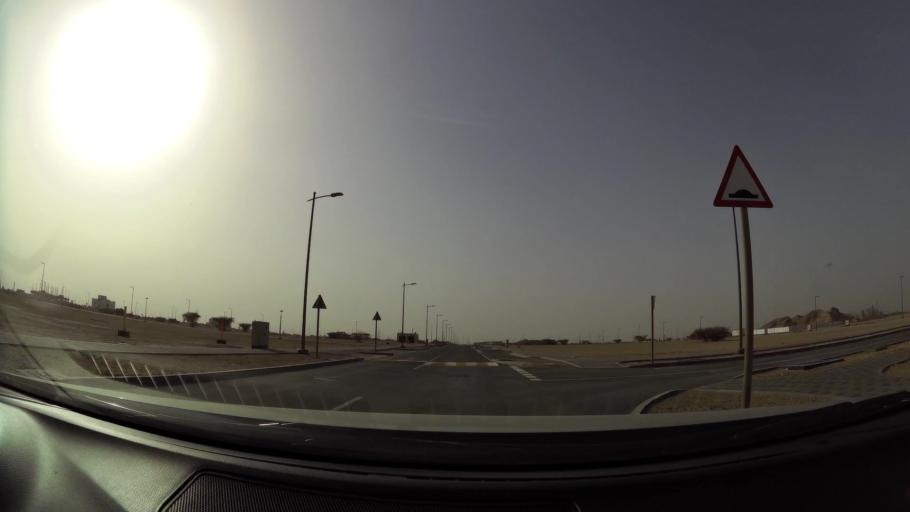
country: AE
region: Abu Dhabi
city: Al Ain
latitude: 24.1187
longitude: 55.7243
